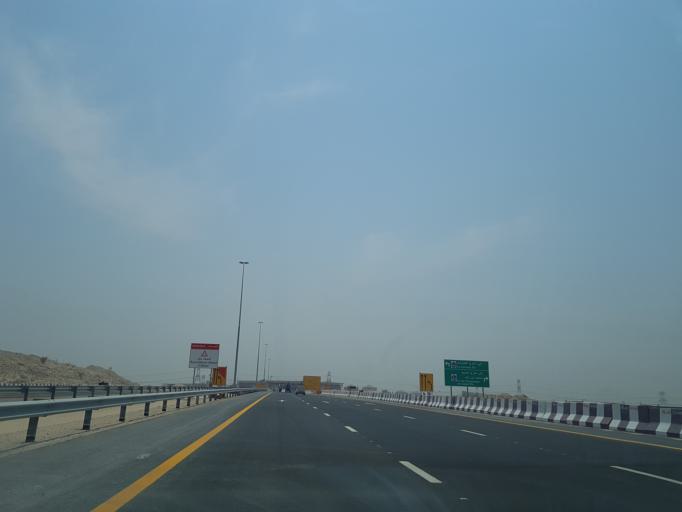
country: AE
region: Dubai
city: Dubai
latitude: 25.0019
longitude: 55.1902
